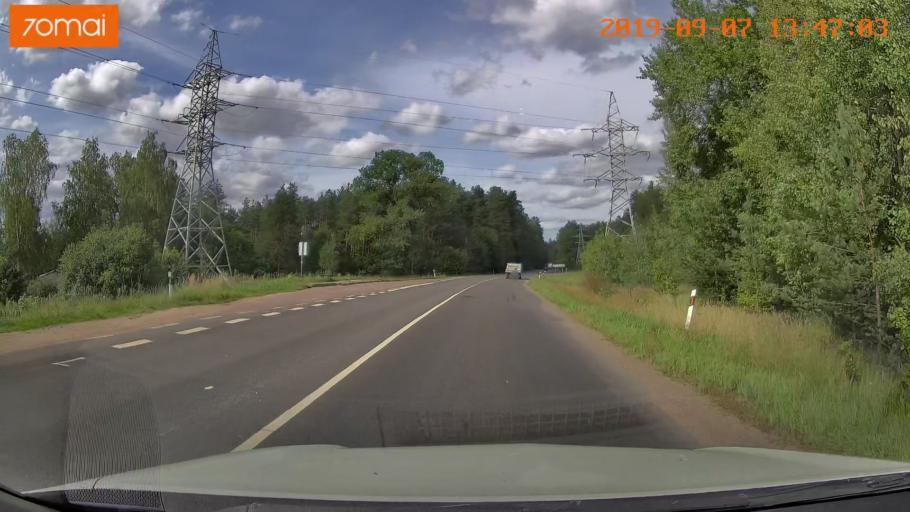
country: LT
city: Baltoji Voke
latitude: 54.5940
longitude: 25.2196
